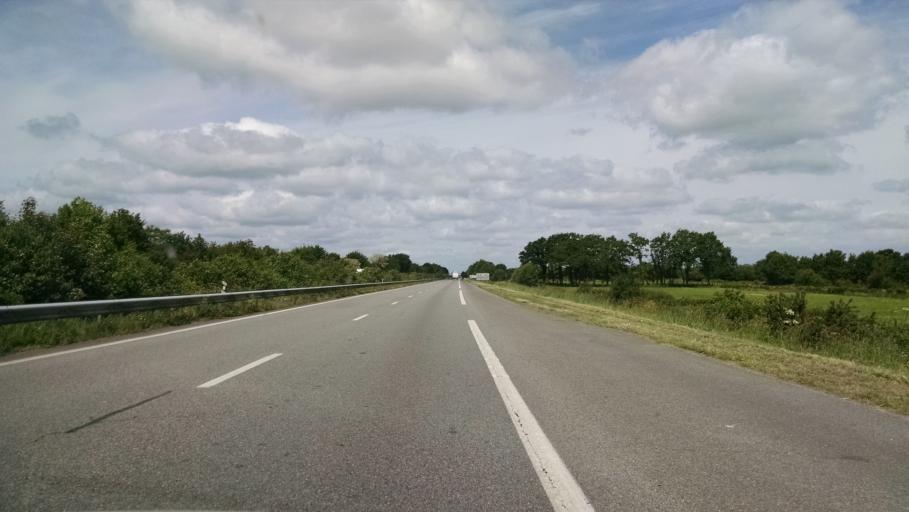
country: FR
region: Pays de la Loire
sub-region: Departement de la Loire-Atlantique
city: La Chapelle-Launay
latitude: 47.3849
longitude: -1.9767
